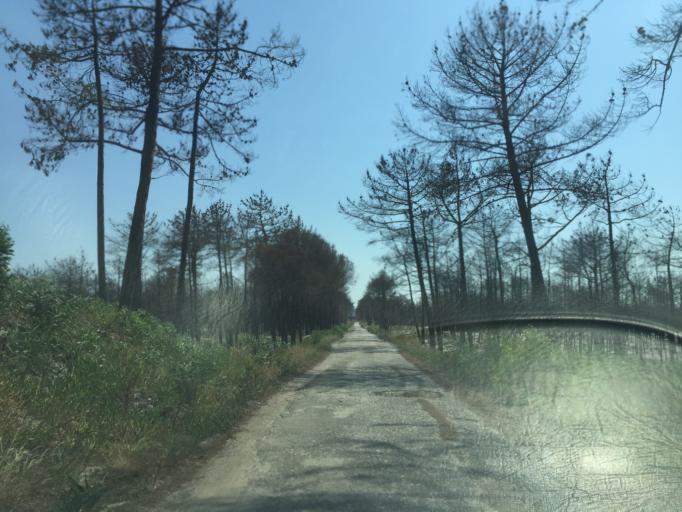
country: PT
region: Coimbra
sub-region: Figueira da Foz
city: Alhadas
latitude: 40.2685
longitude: -8.8314
